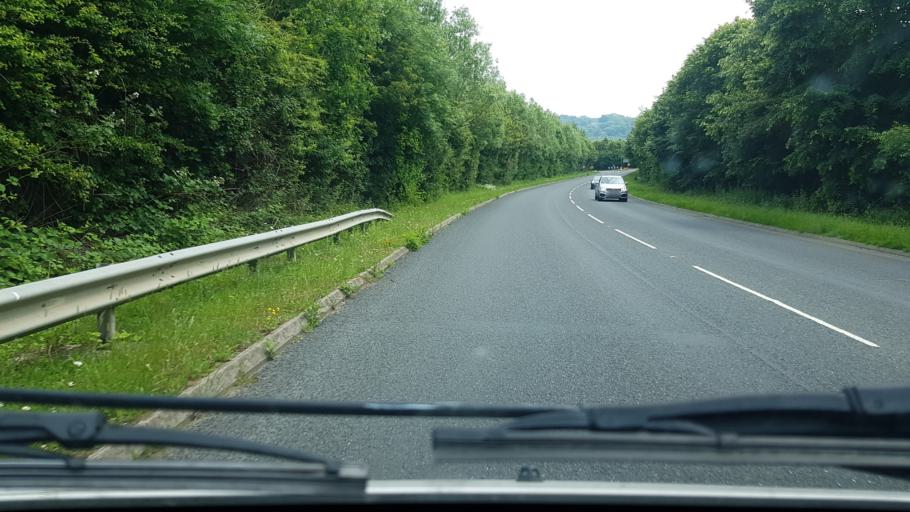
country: GB
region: England
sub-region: Worcestershire
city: Broadway
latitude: 52.0485
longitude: -1.8604
